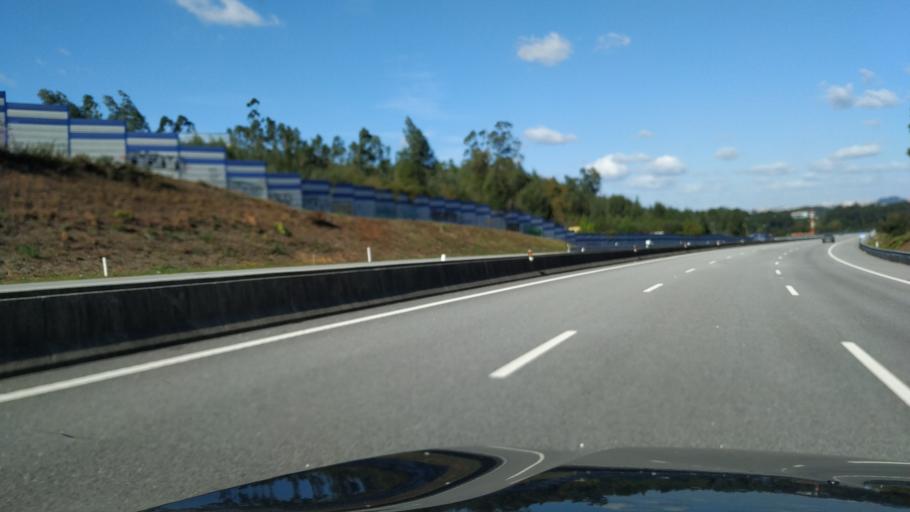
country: PT
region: Porto
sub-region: Vila Nova de Gaia
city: Olival
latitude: 41.0822
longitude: -8.5505
